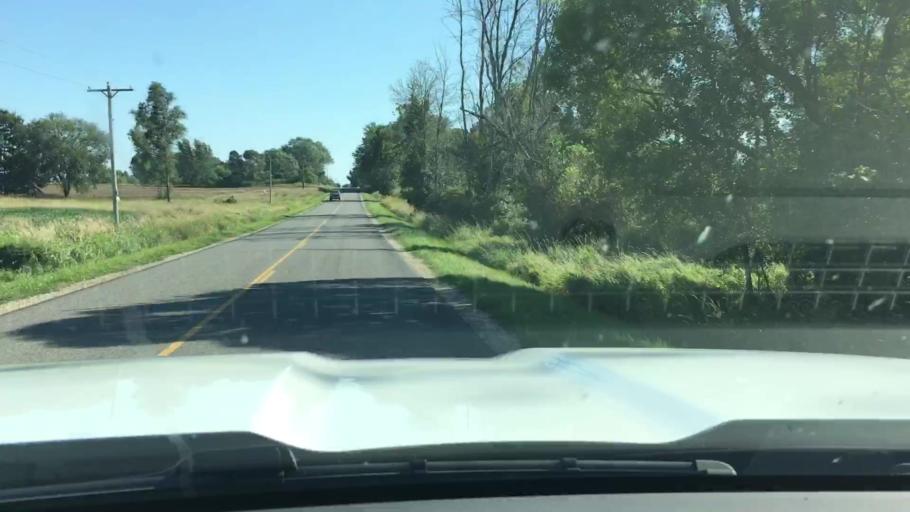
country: US
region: Michigan
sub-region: Muskegon County
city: Ravenna
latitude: 43.2480
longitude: -85.9180
